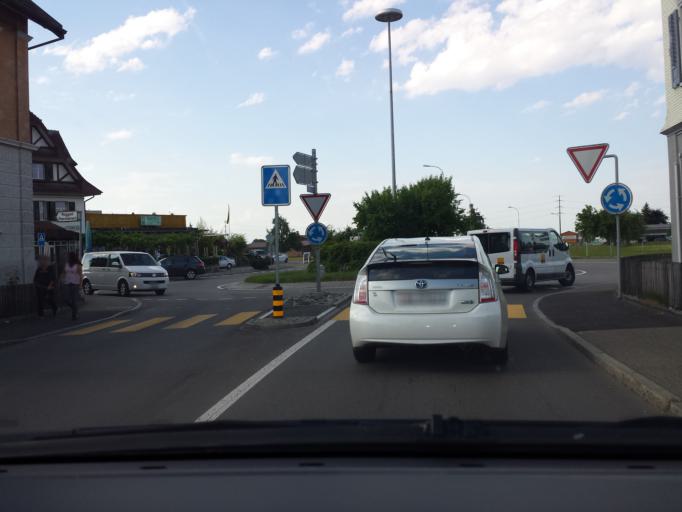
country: CH
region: Saint Gallen
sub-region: Wahlkreis Rorschach
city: Horn
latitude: 47.4859
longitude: 9.4545
